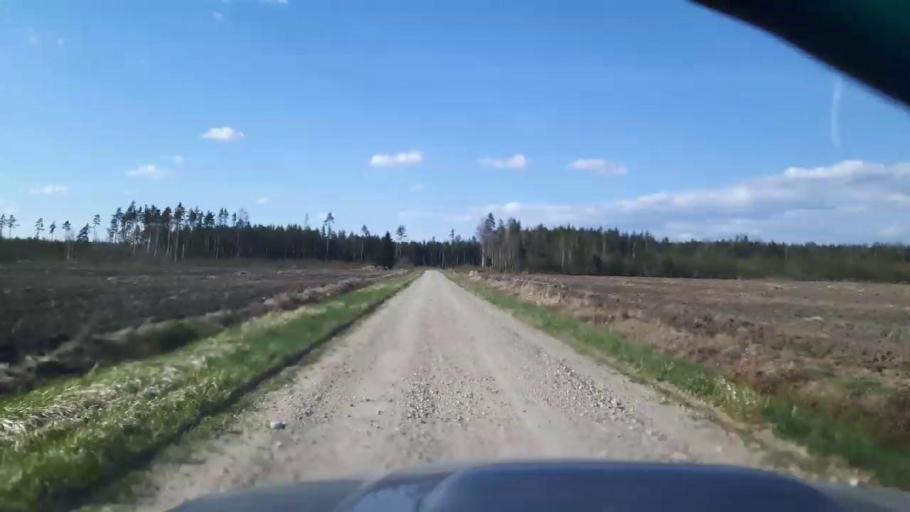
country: EE
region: Paernumaa
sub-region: Tootsi vald
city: Tootsi
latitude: 58.4189
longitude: 24.8521
